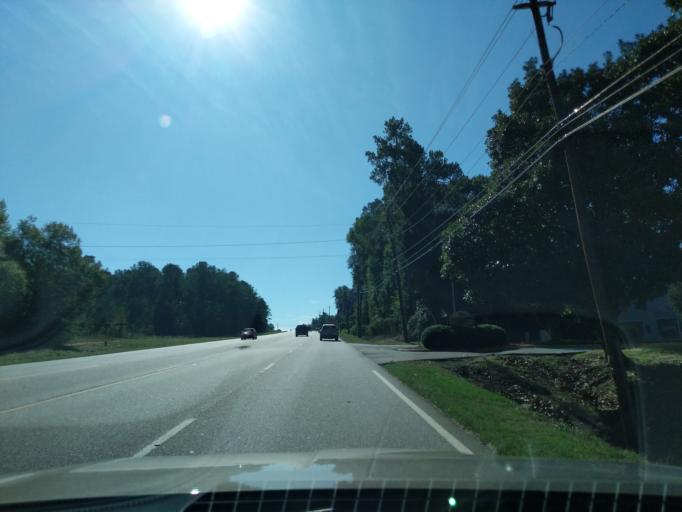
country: US
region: Georgia
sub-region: Richmond County
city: Augusta
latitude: 33.3802
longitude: -82.0022
